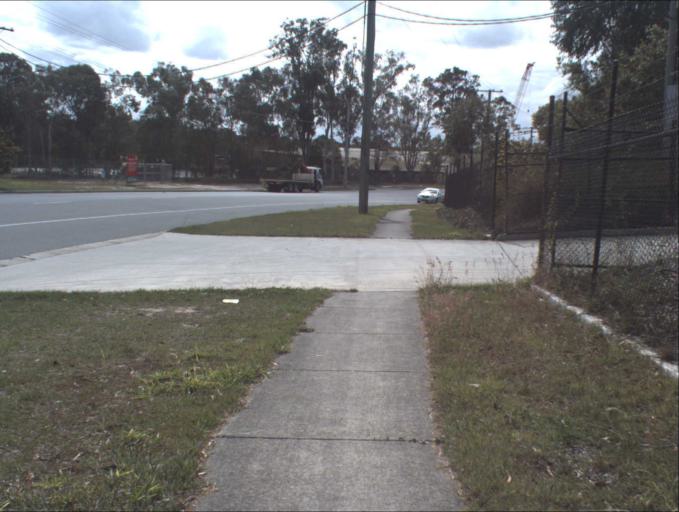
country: AU
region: Queensland
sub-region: Logan
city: Logan Reserve
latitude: -27.6795
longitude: 153.0713
